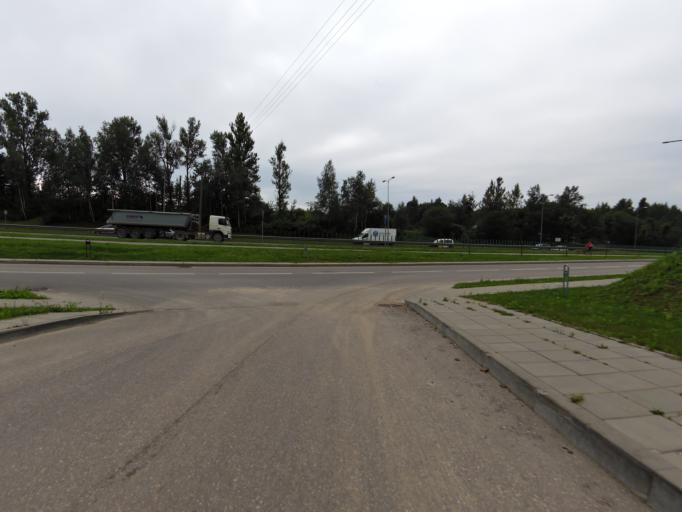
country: LT
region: Vilnius County
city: Naujamiestis
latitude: 54.6566
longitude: 25.2882
